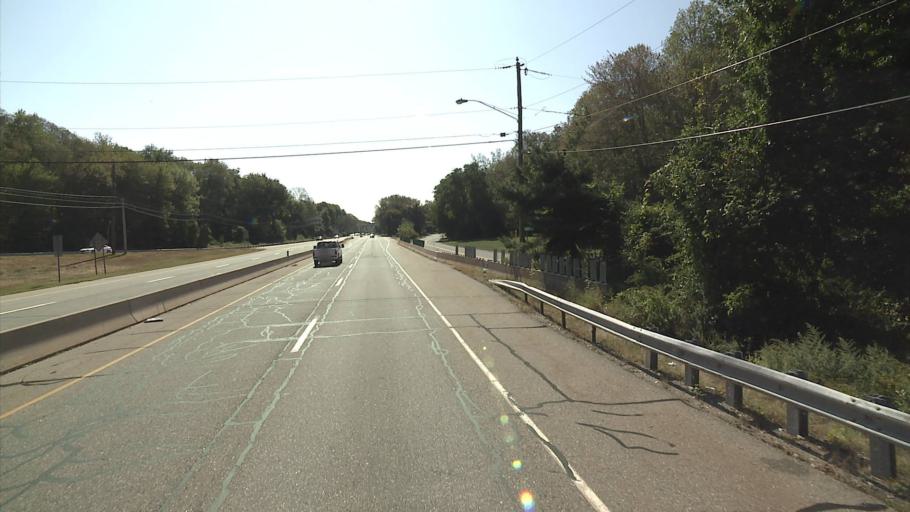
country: US
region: Connecticut
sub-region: New London County
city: Uncasville
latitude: 41.4158
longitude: -72.1095
